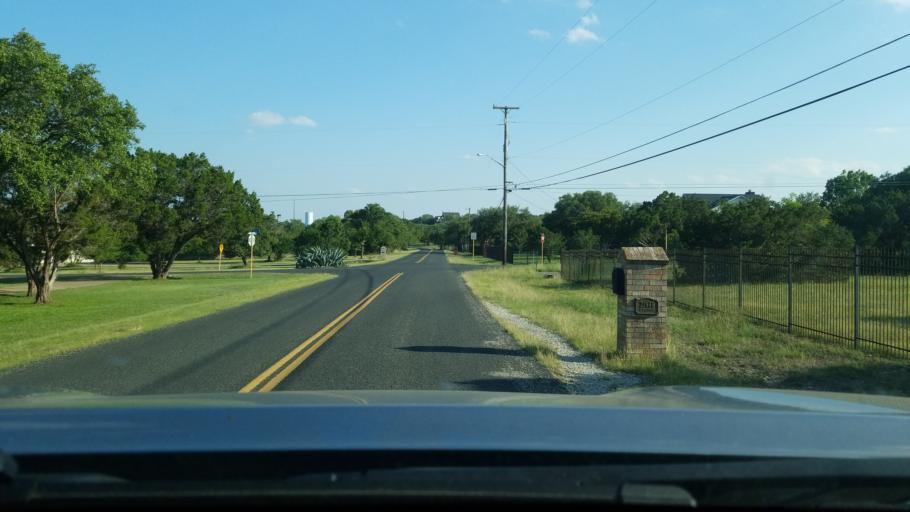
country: US
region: Texas
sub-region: Bexar County
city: Timberwood Park
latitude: 29.7057
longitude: -98.4377
